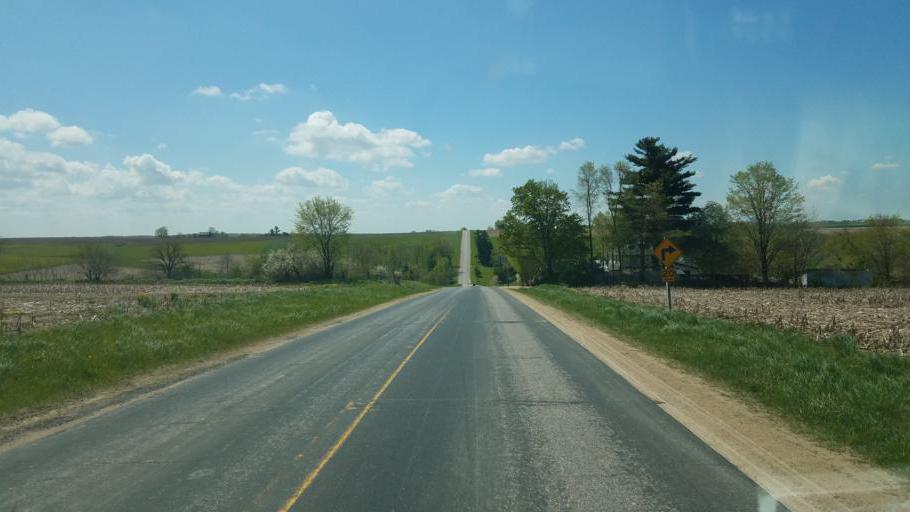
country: US
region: Wisconsin
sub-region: Vernon County
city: Hillsboro
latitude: 43.5840
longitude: -90.3621
